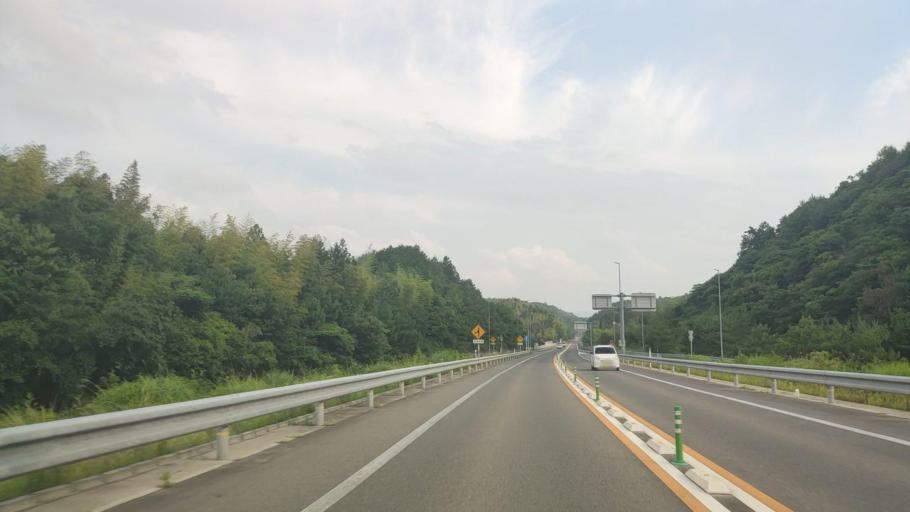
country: JP
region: Tottori
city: Kurayoshi
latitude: 35.4651
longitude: 133.8087
